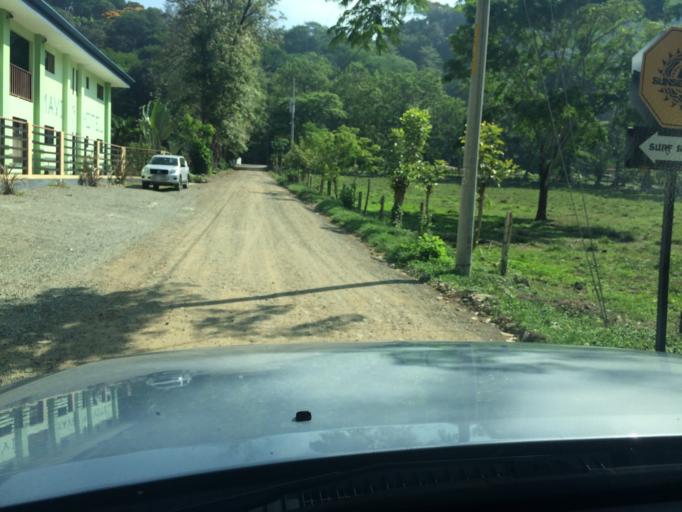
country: CR
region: San Jose
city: San Isidro
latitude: 9.2524
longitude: -83.8614
